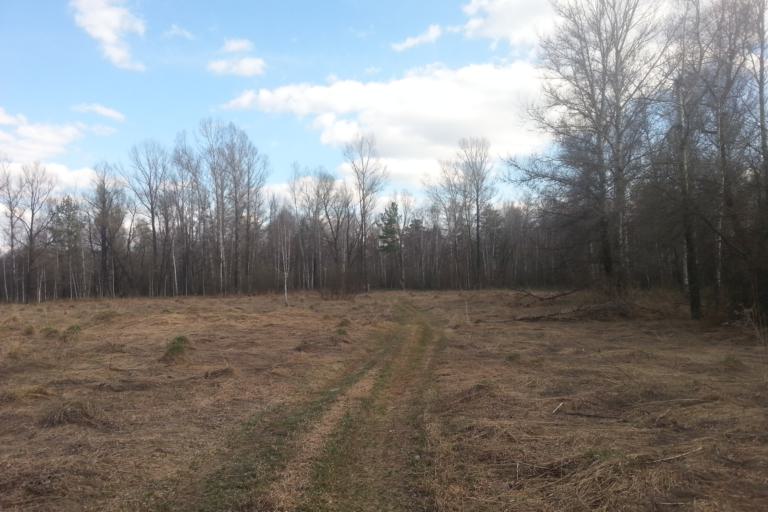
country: RU
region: Altai Krai
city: Sannikovo
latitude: 53.3323
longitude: 84.0200
